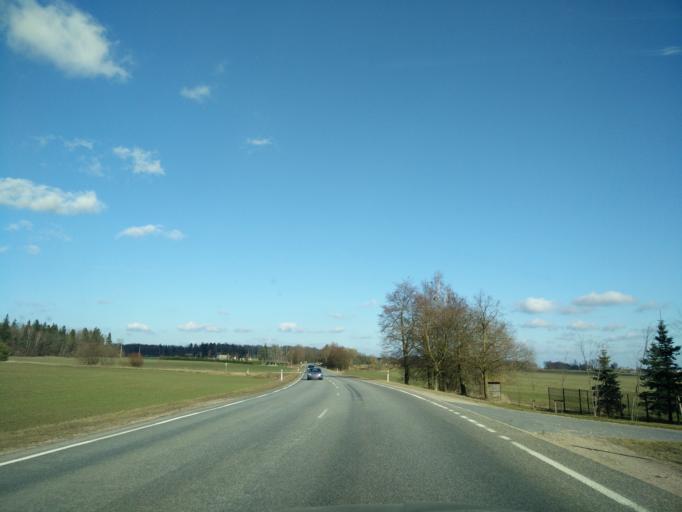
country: LT
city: Kulautuva
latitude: 54.9526
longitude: 23.7142
